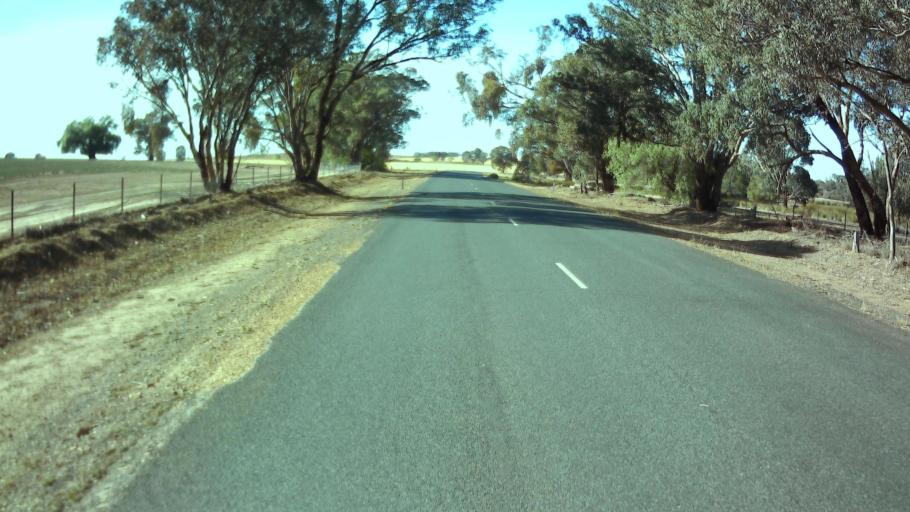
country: AU
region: New South Wales
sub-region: Weddin
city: Grenfell
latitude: -33.9832
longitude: 148.1406
